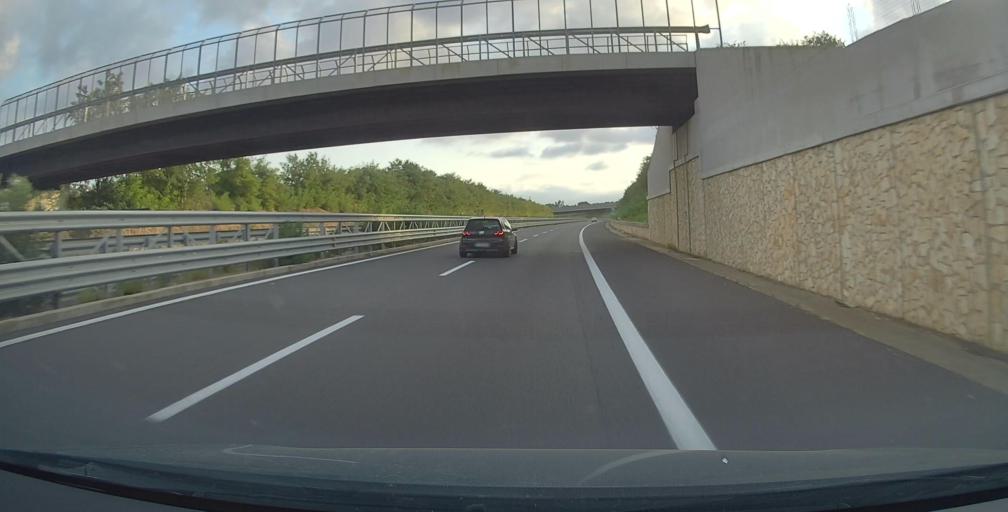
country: IT
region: Calabria
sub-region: Provincia di Catanzaro
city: Acconia
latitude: 38.8641
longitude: 16.2773
